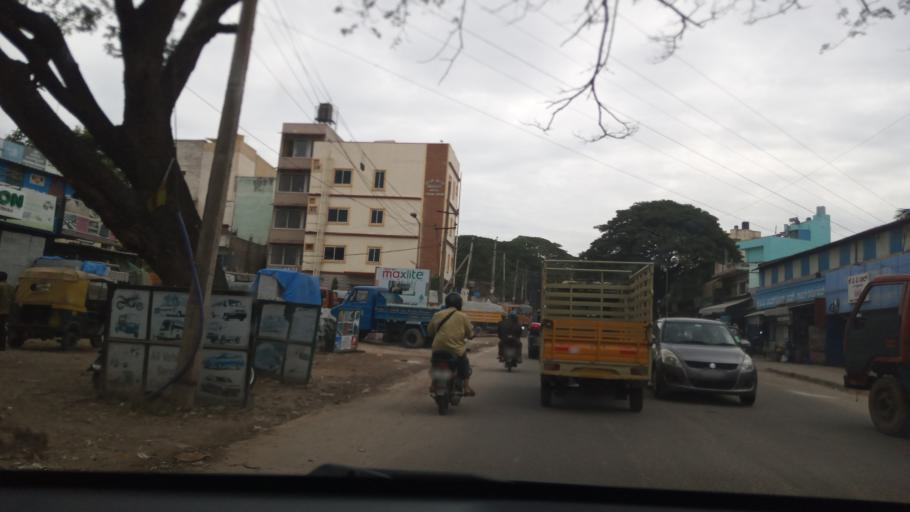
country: IN
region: Karnataka
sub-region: Bangalore Urban
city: Bangalore
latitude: 13.0196
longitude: 77.5388
